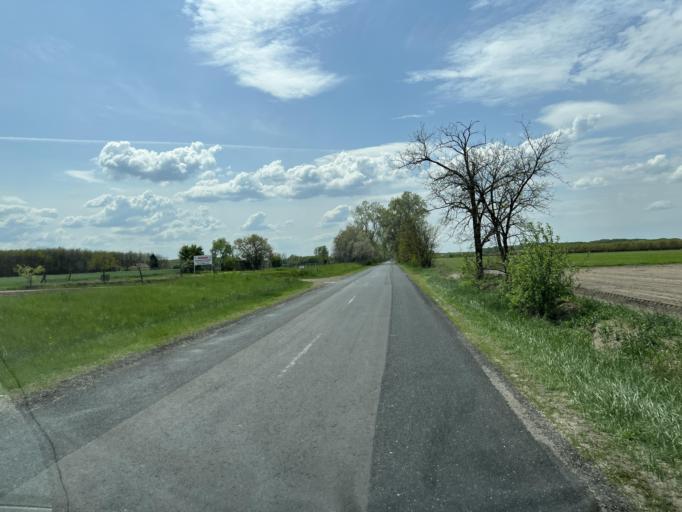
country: HU
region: Pest
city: Cegled
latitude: 47.1486
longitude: 19.7557
